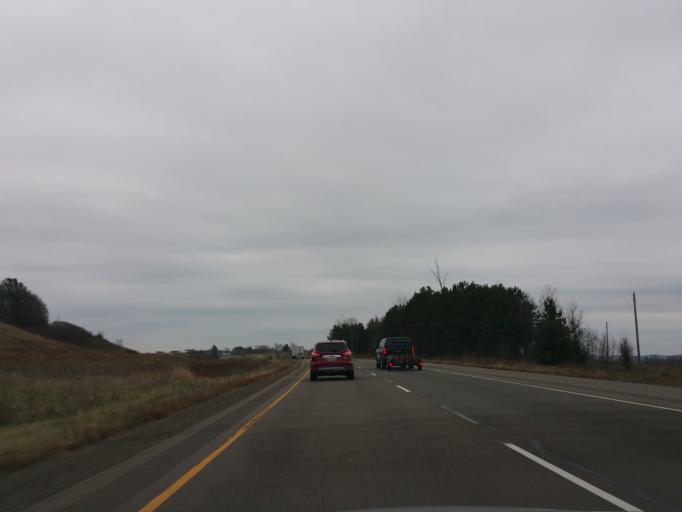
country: US
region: Wisconsin
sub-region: Trempealeau County
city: Blair
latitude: 44.4157
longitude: -91.0494
